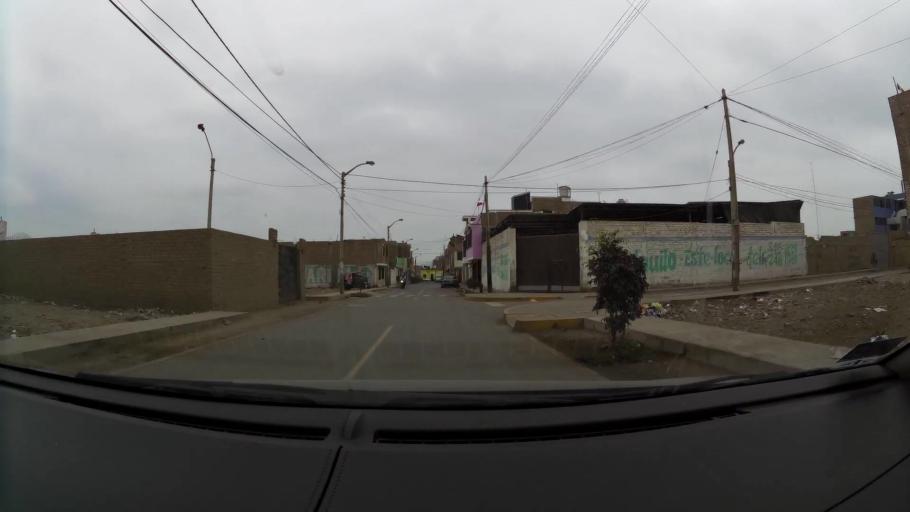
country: PE
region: Lima
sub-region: Provincia de Huaral
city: Huaral
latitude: -11.4914
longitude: -77.2018
